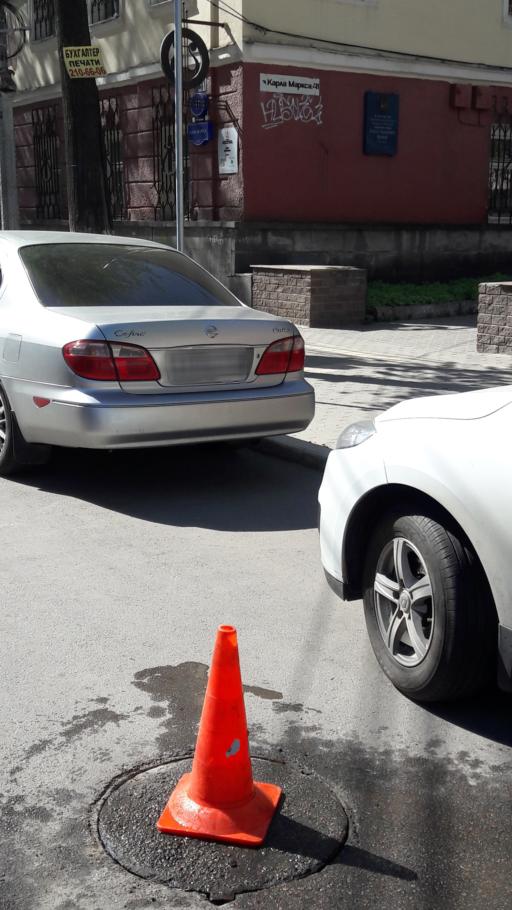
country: RU
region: Voronezj
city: Voronezh
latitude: 51.6607
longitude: 39.2078
